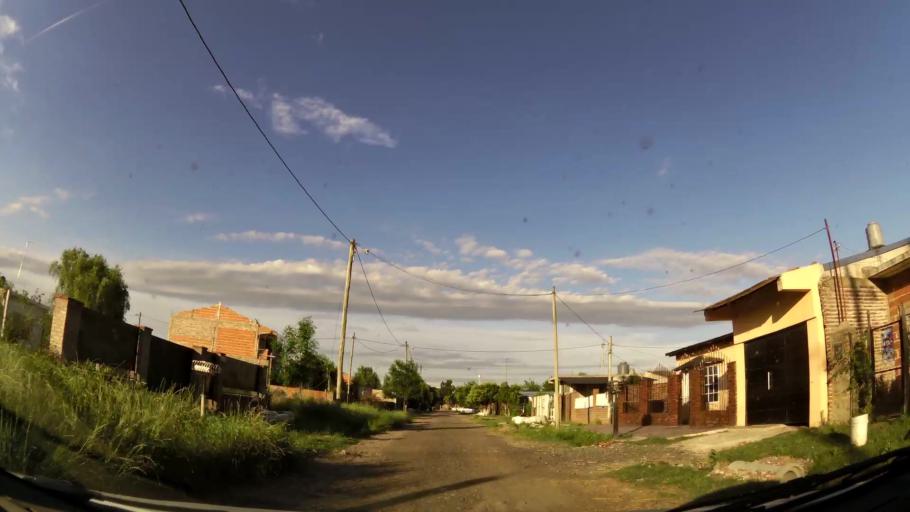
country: AR
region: Buenos Aires
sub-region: Partido de Merlo
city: Merlo
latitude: -34.7000
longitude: -58.7530
